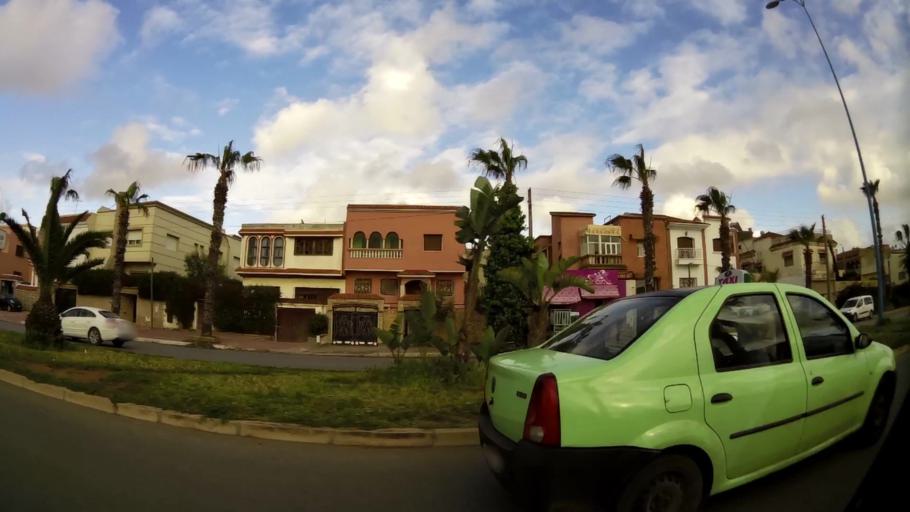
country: MA
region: Grand Casablanca
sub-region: Mohammedia
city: Mohammedia
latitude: 33.6985
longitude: -7.3708
